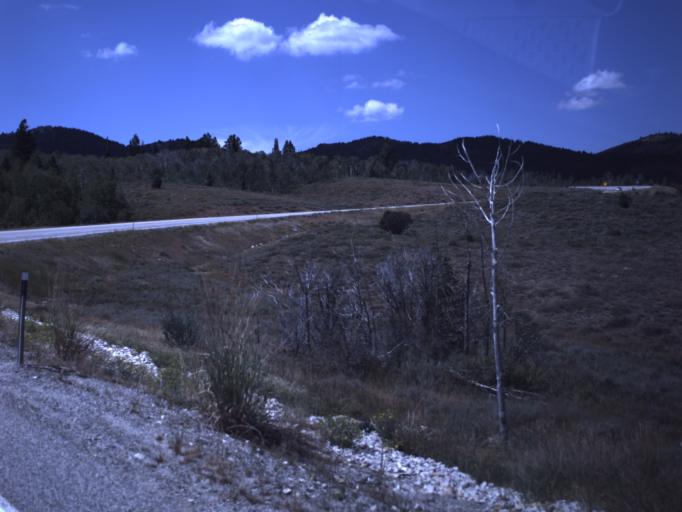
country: US
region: Idaho
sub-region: Bear Lake County
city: Paris
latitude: 41.9291
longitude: -111.4424
